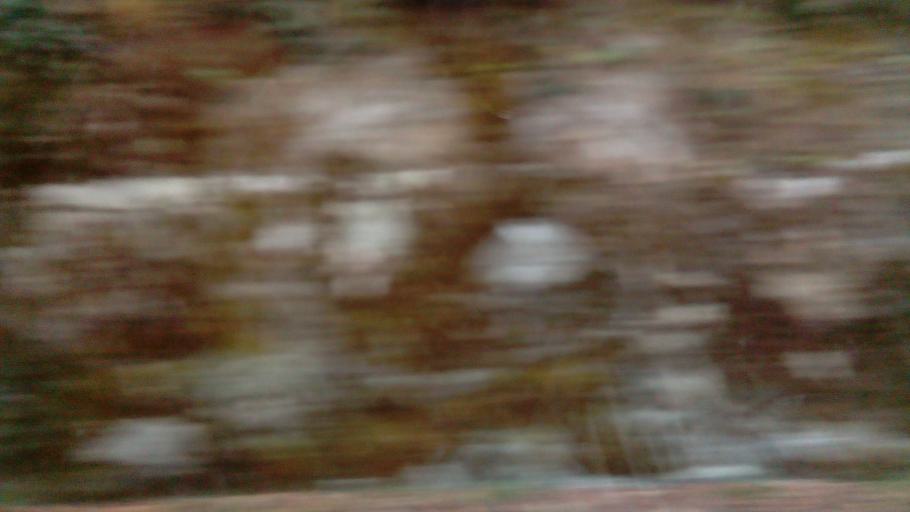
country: TW
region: Taiwan
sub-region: Hualien
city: Hualian
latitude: 24.3479
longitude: 121.3170
